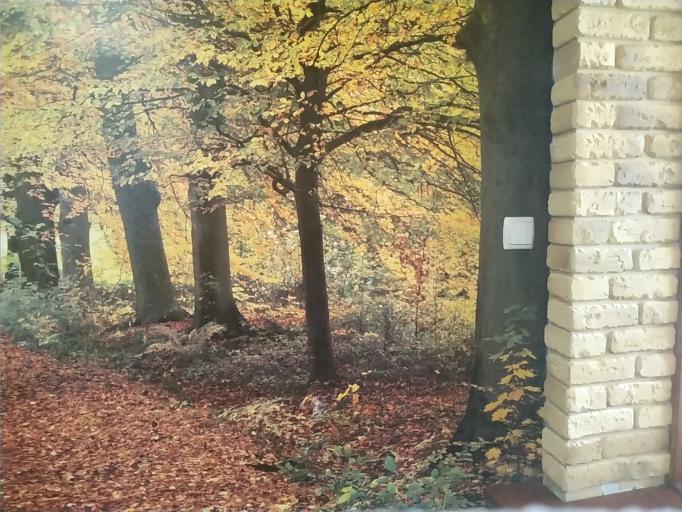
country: RU
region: Tverskaya
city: Vyshniy Volochek
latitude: 57.6341
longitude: 34.5703
